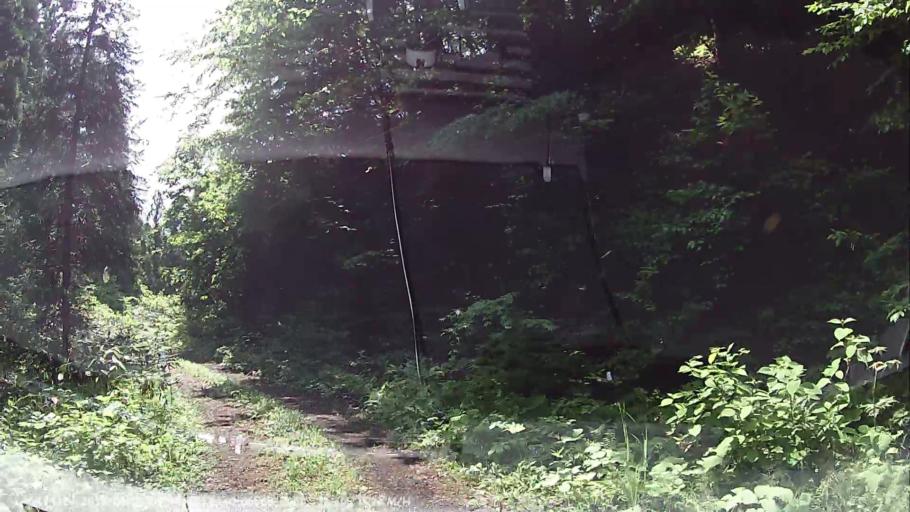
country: JP
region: Fukushima
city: Inawashiro
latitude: 37.3880
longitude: 140.0606
